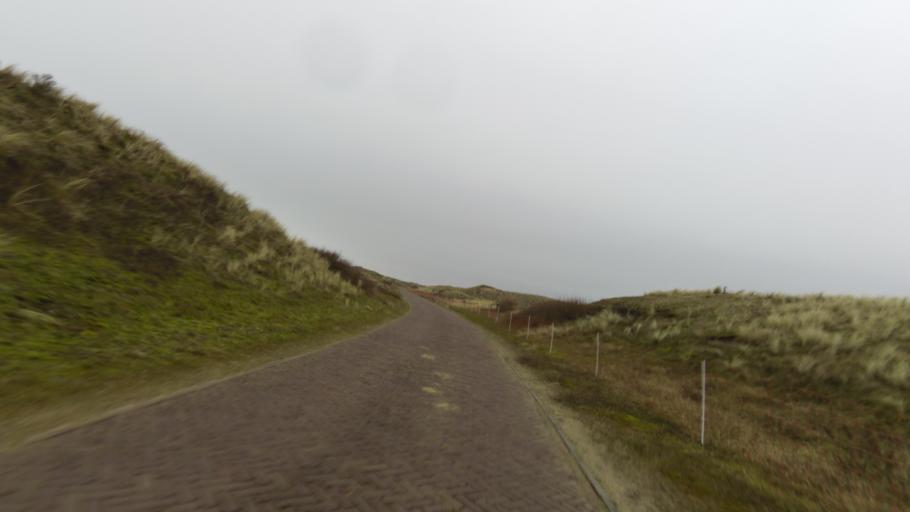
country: NL
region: North Holland
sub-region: Gemeente Beverwijk
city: Beverwijk
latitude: 52.5245
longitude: 4.6029
